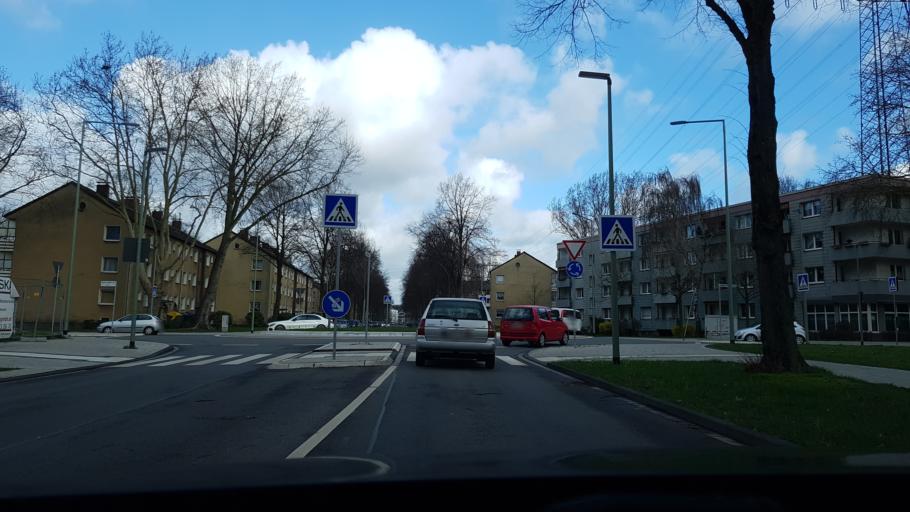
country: DE
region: North Rhine-Westphalia
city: Meiderich
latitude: 51.5085
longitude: 6.7856
